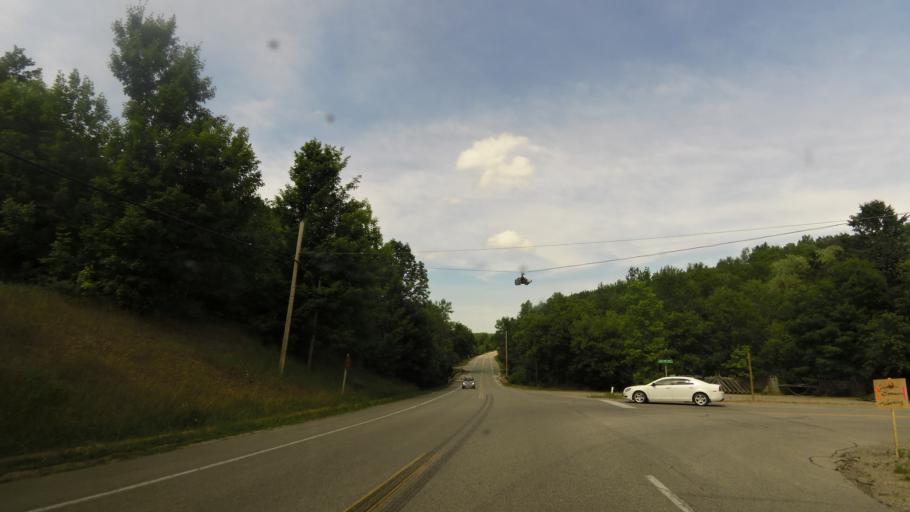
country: CA
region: Ontario
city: Orangeville
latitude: 43.9823
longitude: -80.0458
